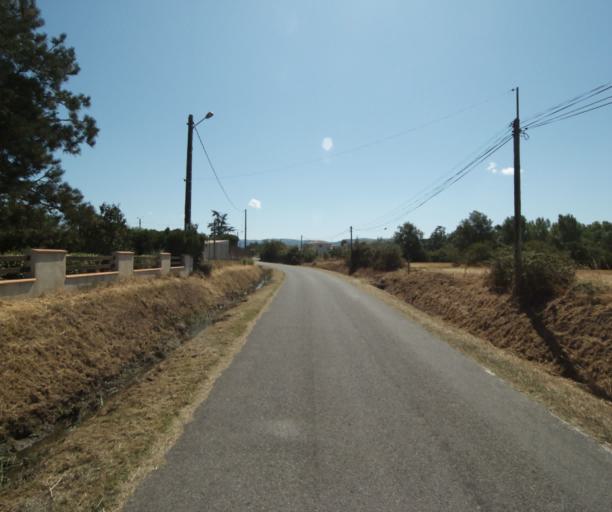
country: FR
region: Midi-Pyrenees
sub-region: Departement de la Haute-Garonne
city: Revel
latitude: 43.4725
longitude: 1.9905
